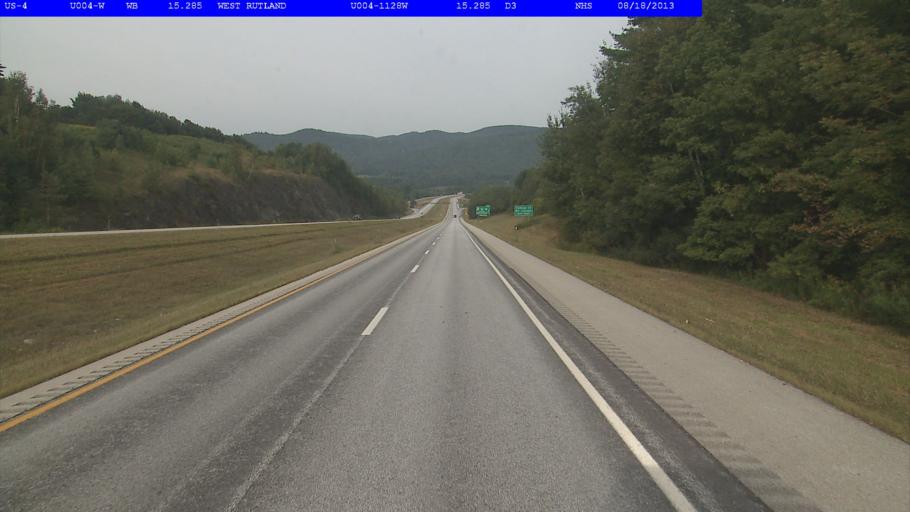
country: US
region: Vermont
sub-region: Rutland County
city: West Rutland
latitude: 43.5904
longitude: -73.0307
